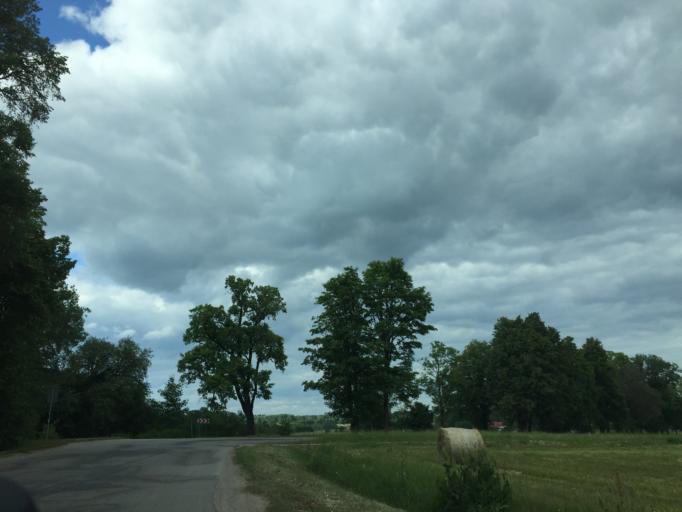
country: LV
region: Skriveri
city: Skriveri
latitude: 56.8356
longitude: 25.1323
